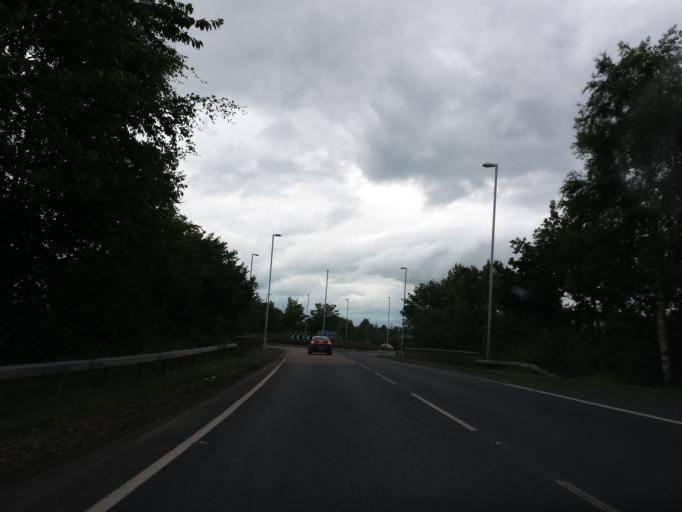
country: GB
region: Scotland
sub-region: Dumfries and Galloway
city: Dumfries
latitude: 55.0640
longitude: -3.6484
